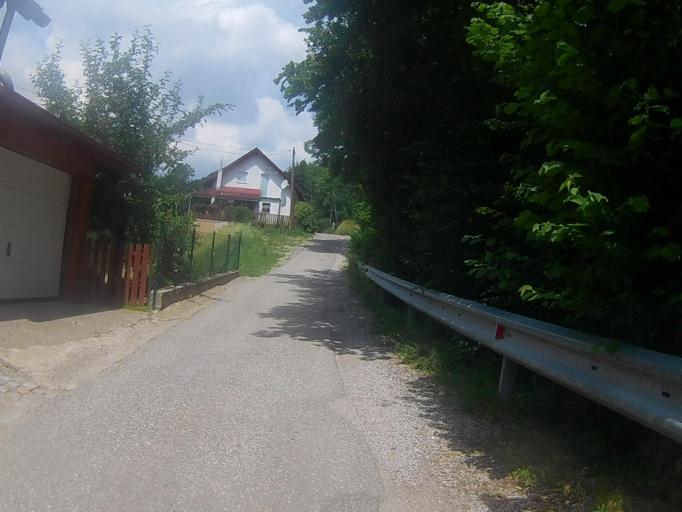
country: SI
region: Maribor
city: Bresternica
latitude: 46.5892
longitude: 15.5892
